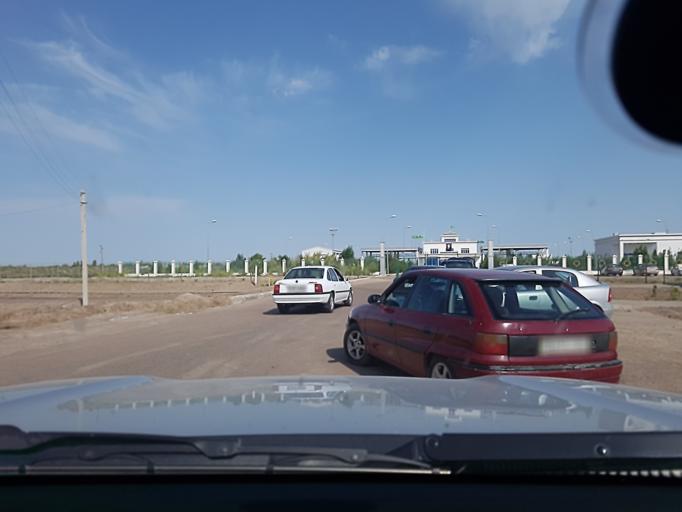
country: TM
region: Dasoguz
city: Dasoguz
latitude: 41.7742
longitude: 60.0567
